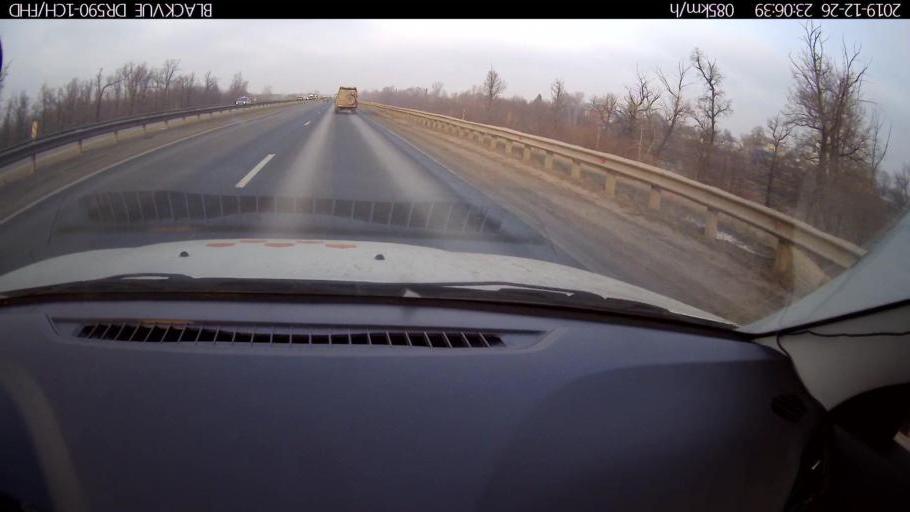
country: RU
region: Nizjnij Novgorod
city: Gorbatovka
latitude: 56.2073
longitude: 43.7520
